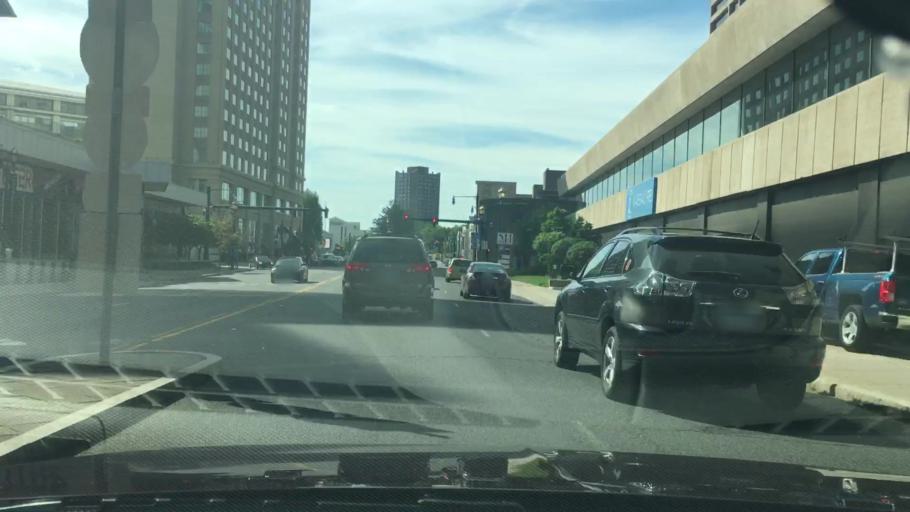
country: US
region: Connecticut
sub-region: Hartford County
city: Hartford
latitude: 41.7653
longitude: -72.6697
